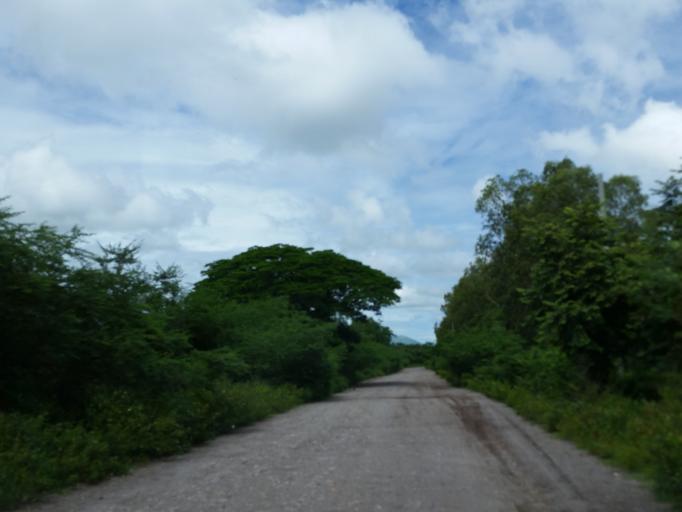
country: NI
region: Leon
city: Telica
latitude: 12.6687
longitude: -86.7959
